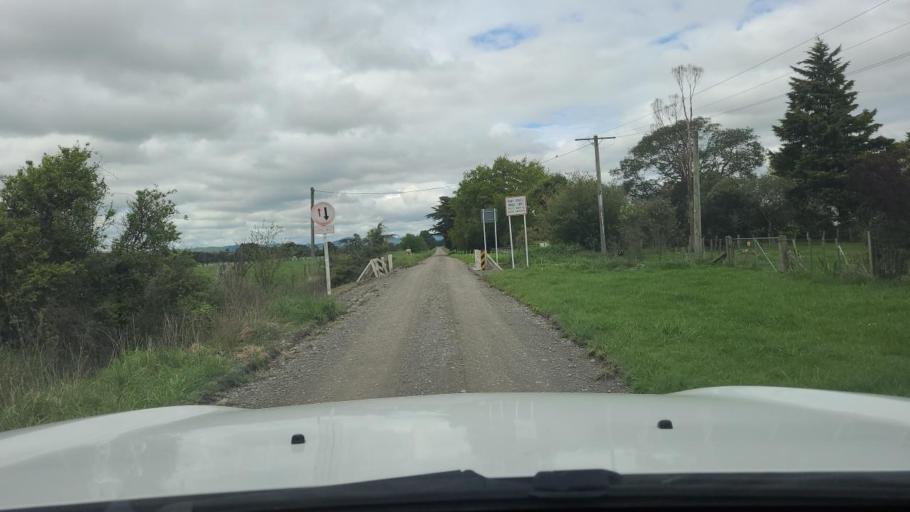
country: NZ
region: Wellington
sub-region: South Wairarapa District
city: Waipawa
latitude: -41.1460
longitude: 175.3811
